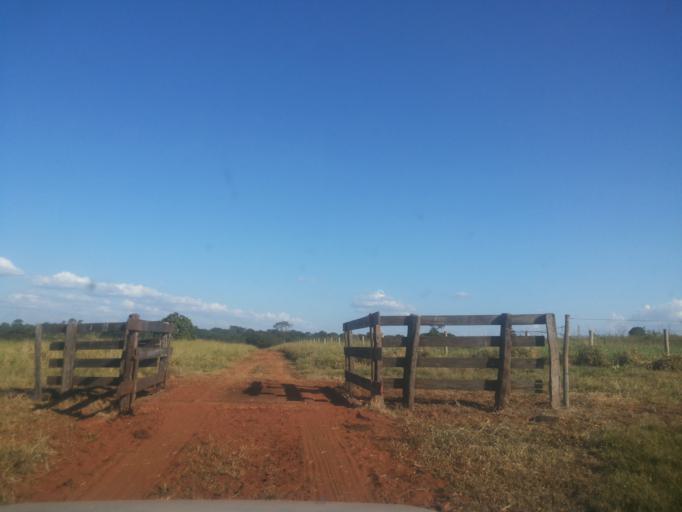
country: BR
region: Minas Gerais
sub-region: Santa Vitoria
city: Santa Vitoria
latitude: -19.0057
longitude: -50.4544
